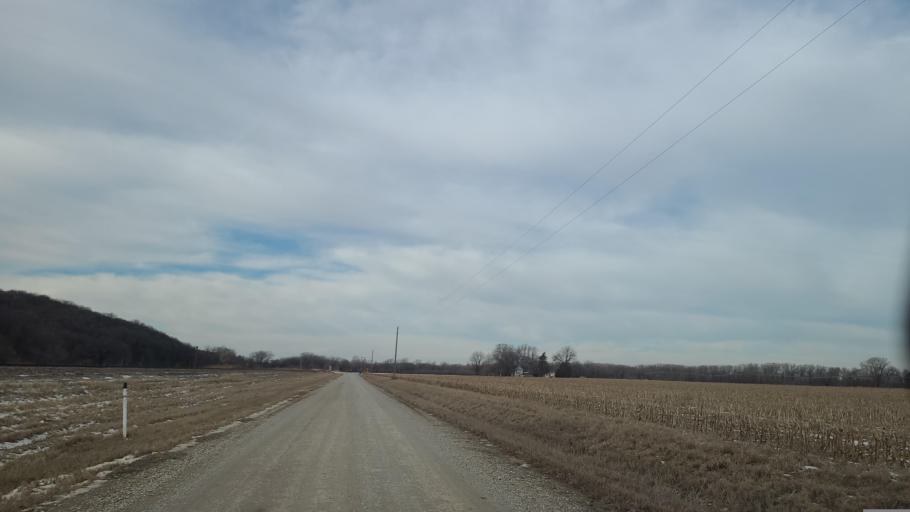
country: US
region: Kansas
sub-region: Jefferson County
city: Oskaloosa
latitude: 39.0600
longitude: -95.4557
